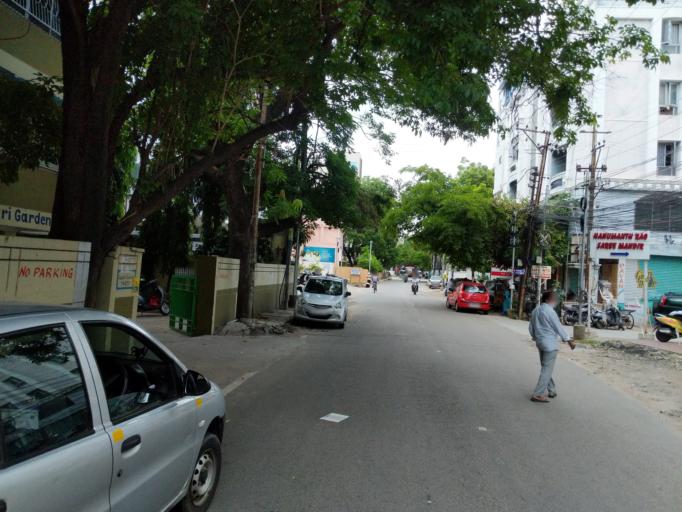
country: IN
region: Telangana
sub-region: Hyderabad
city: Hyderabad
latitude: 17.4373
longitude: 78.4527
